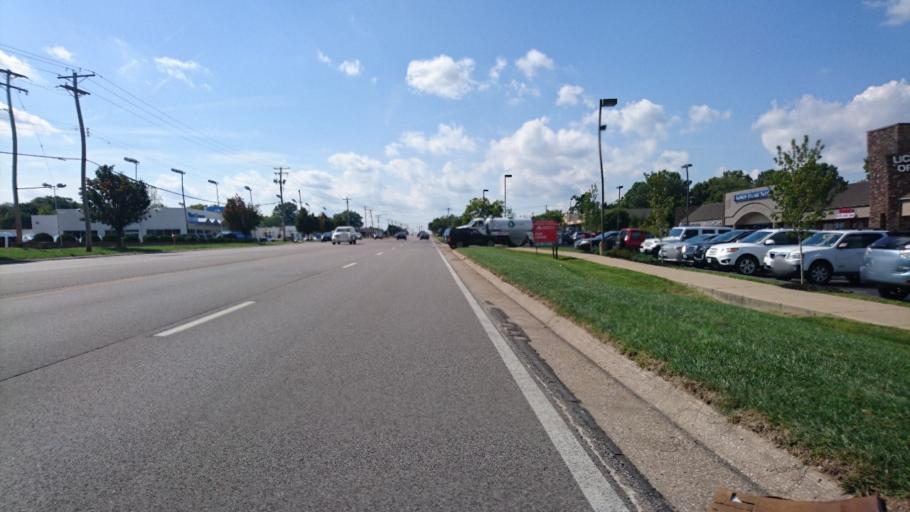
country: US
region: Missouri
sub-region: Saint Louis County
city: Ellisville
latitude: 38.5929
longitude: -90.5687
